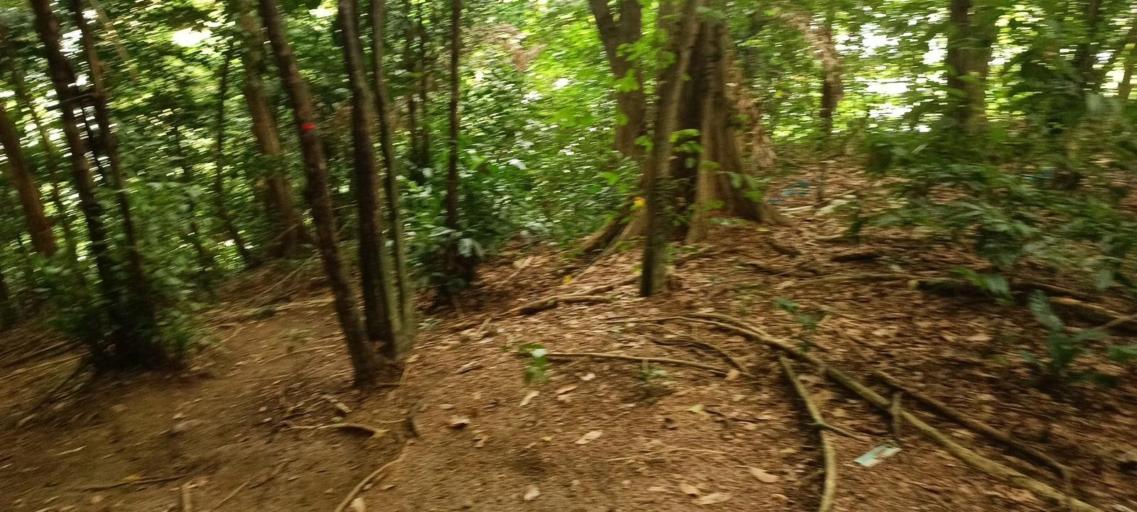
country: MY
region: Penang
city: George Town
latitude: 5.3970
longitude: 100.2933
